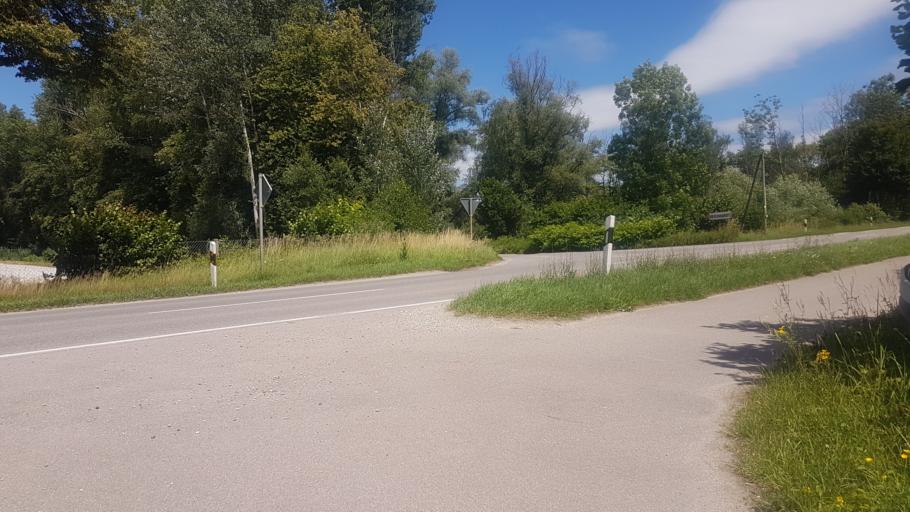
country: DE
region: Bavaria
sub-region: Swabia
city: Hochstadt an der Donau
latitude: 48.6073
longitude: 10.5819
